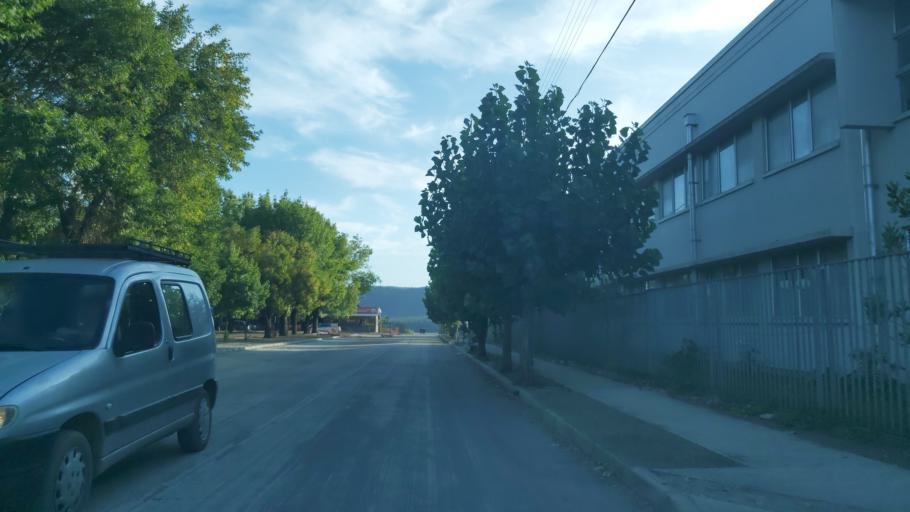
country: CL
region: Biobio
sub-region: Provincia de Biobio
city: La Laja
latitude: -37.1619
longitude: -72.9078
